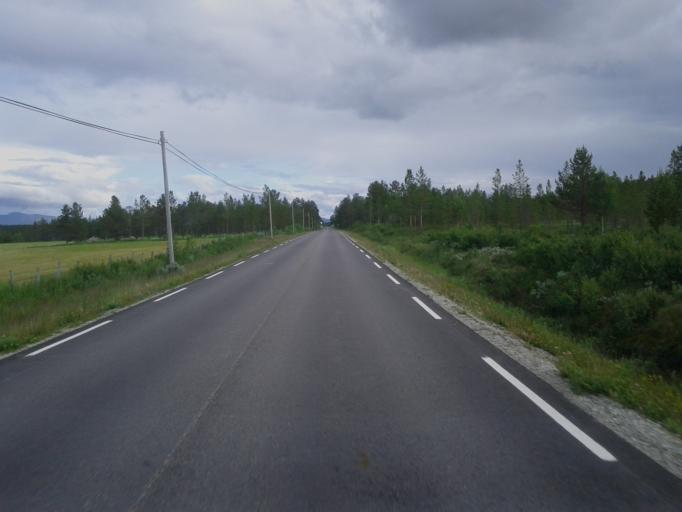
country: NO
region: Sor-Trondelag
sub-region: Roros
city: Roros
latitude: 62.2920
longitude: 11.7299
